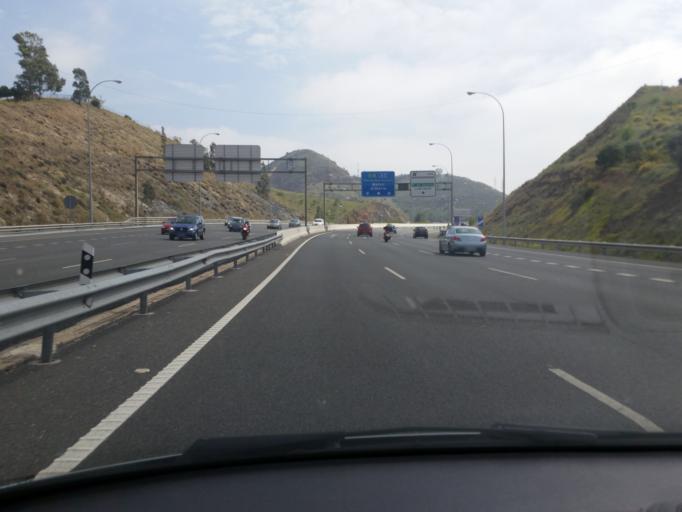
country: ES
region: Andalusia
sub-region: Provincia de Malaga
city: Malaga
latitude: 36.7398
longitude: -4.3985
